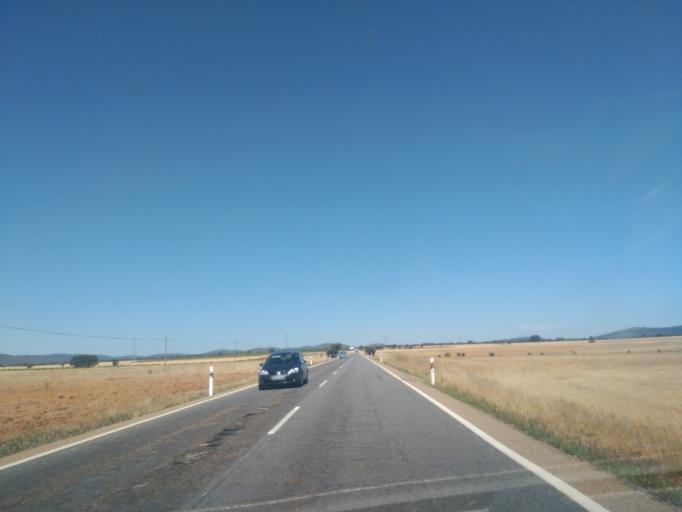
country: ES
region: Castille and Leon
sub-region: Provincia de Zamora
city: Pozuelo de Tabara
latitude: 41.7950
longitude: -5.9102
